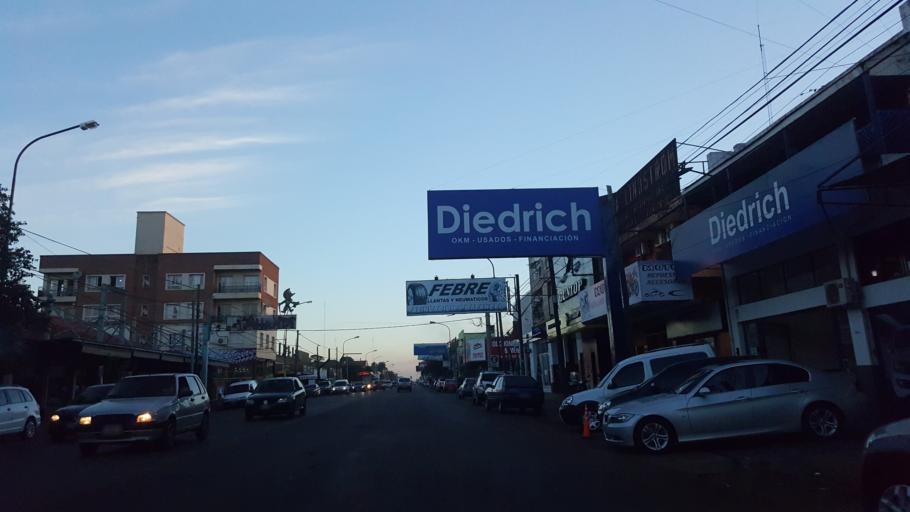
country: AR
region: Misiones
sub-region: Departamento de Capital
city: Posadas
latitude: -27.3946
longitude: -55.9014
